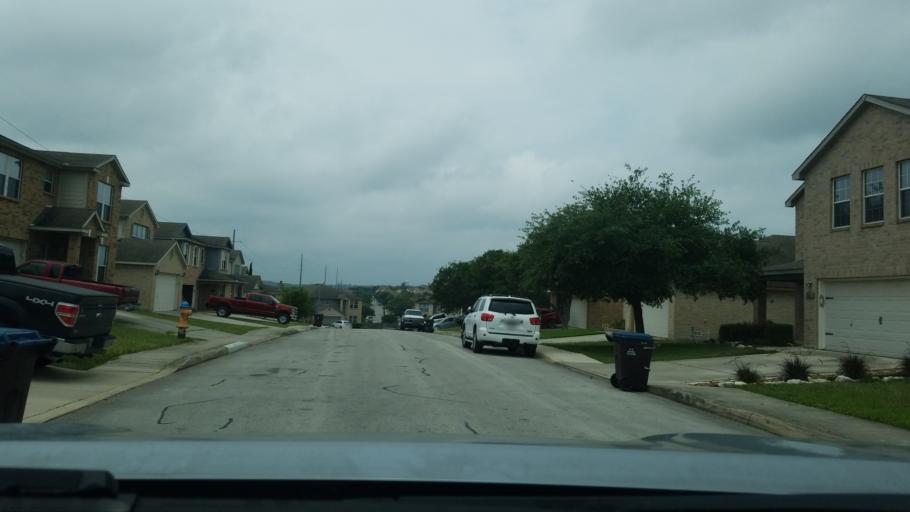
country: US
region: Texas
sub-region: Bexar County
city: Timberwood Park
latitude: 29.6801
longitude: -98.4672
